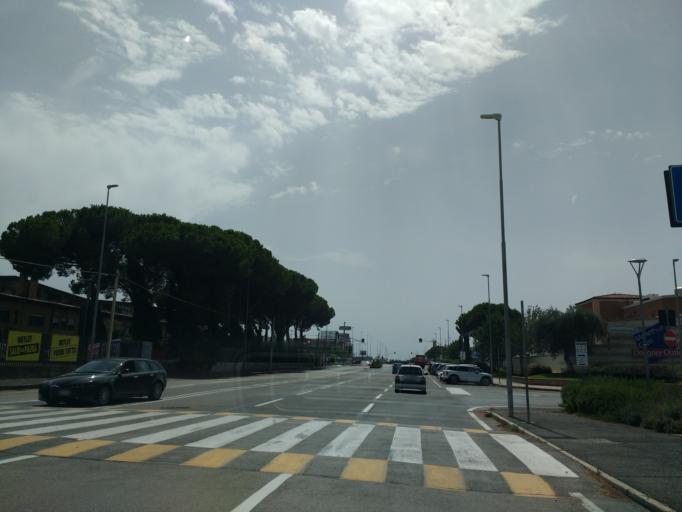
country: IT
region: Latium
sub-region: Citta metropolitana di Roma Capitale
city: Monte Migliore-La Selvotta
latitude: 41.7179
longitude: 12.4472
